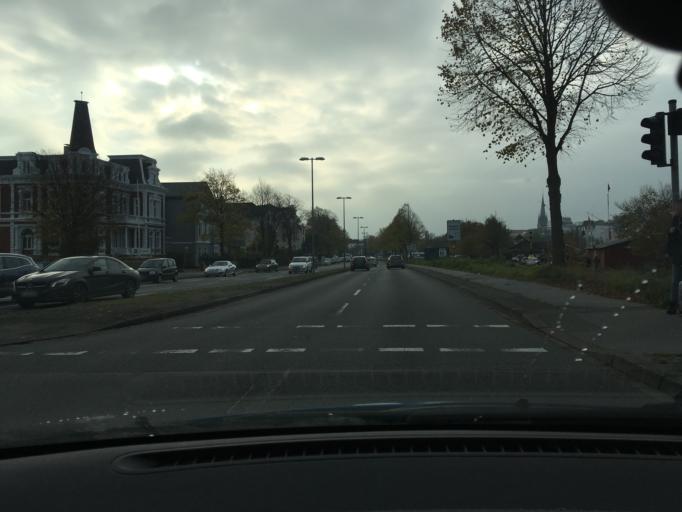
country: DE
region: Schleswig-Holstein
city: Flensburg
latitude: 54.7917
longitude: 9.4382
